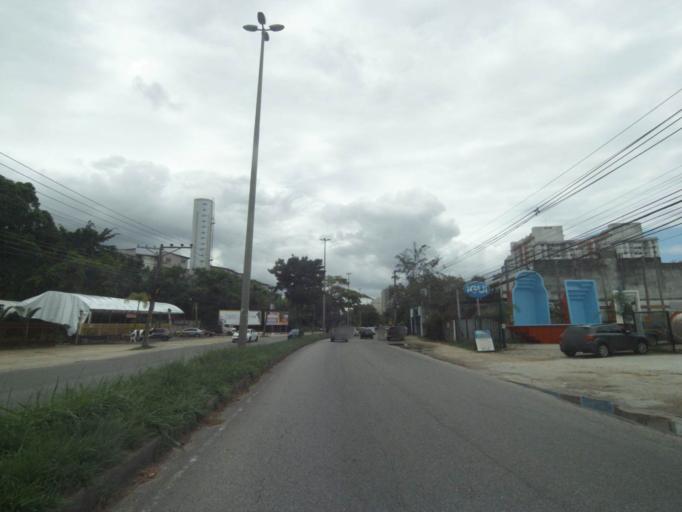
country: BR
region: Rio de Janeiro
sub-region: Nilopolis
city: Nilopolis
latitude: -22.9660
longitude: -43.4111
